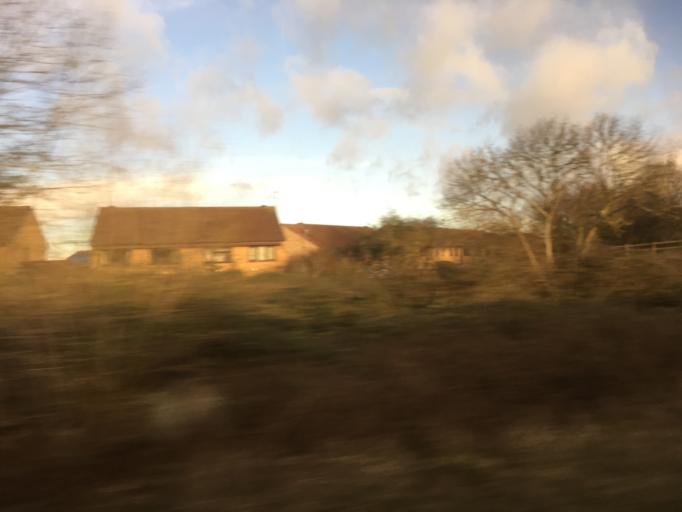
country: GB
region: England
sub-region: South Gloucestershire
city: Yate
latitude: 51.5266
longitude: -2.4116
